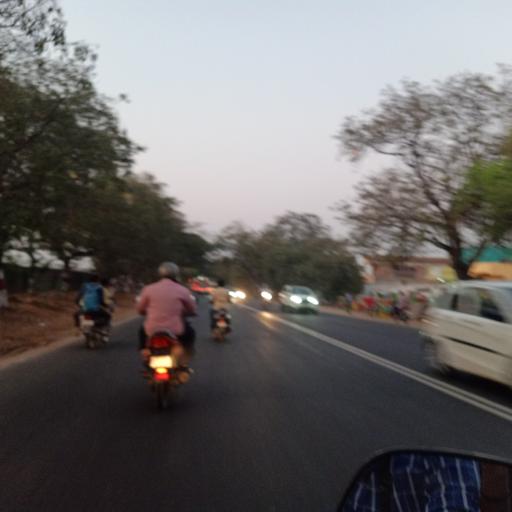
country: IN
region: Telangana
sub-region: Rangareddi
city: Secunderabad
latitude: 17.5482
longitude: 78.5355
